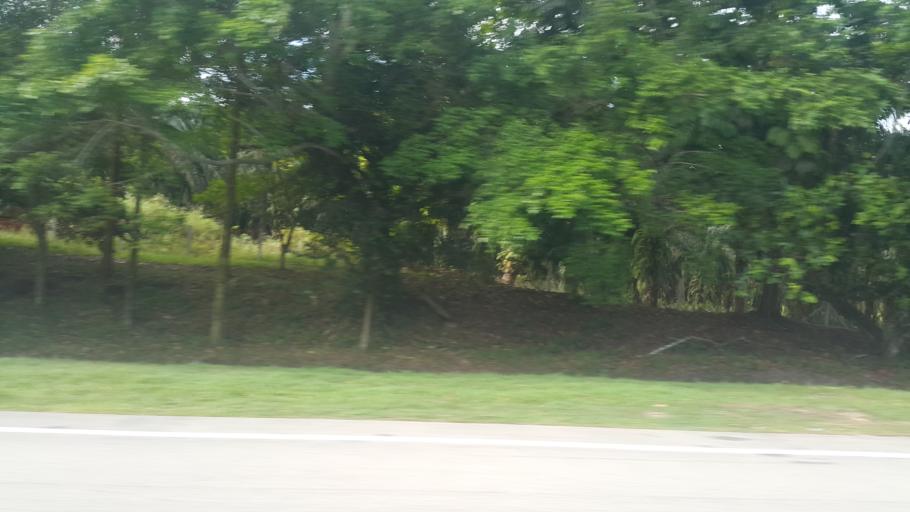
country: MY
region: Johor
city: Taman Senai
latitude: 1.6074
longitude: 103.6136
